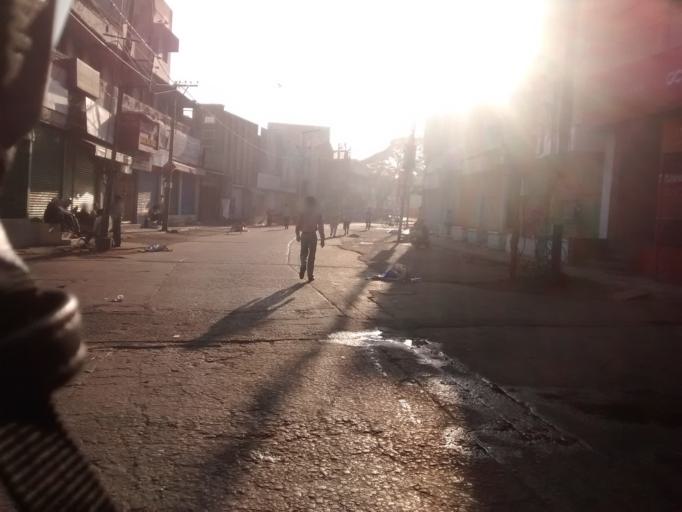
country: IN
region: Telangana
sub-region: Hyderabad
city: Malkajgiri
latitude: 17.4375
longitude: 78.4925
